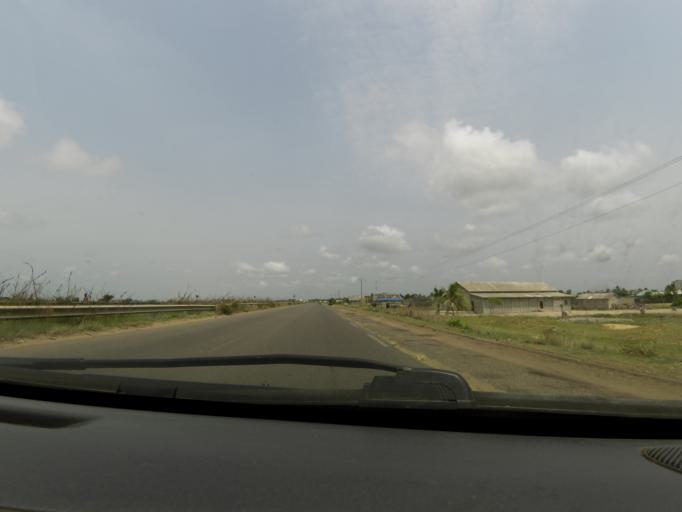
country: BJ
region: Queme
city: Porto-Novo
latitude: 6.3832
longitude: 2.6731
